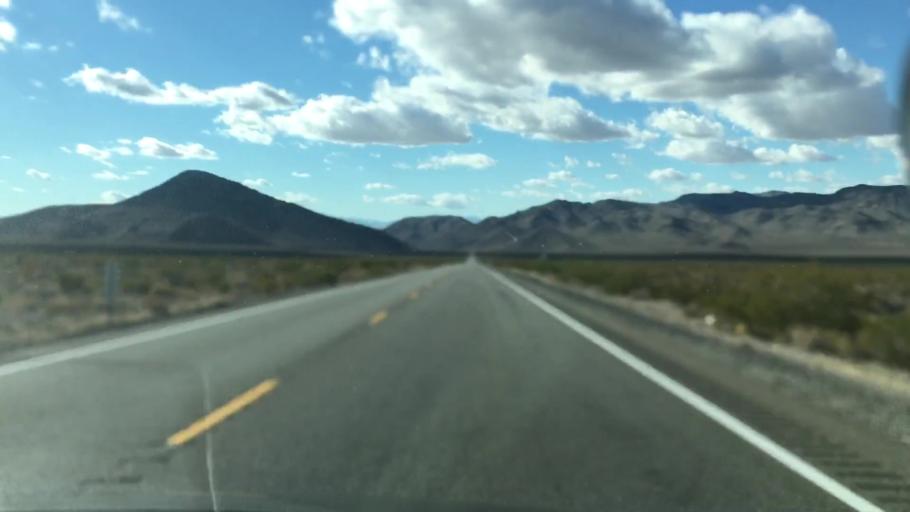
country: US
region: Nevada
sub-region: Nye County
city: Pahrump
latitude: 36.5934
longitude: -116.0225
